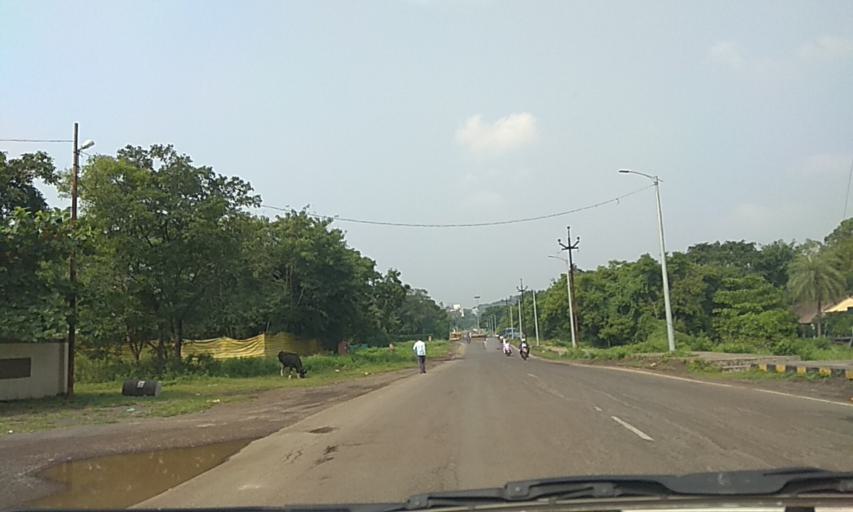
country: IN
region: Maharashtra
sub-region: Pune Division
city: Shivaji Nagar
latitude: 18.5450
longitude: 73.8457
